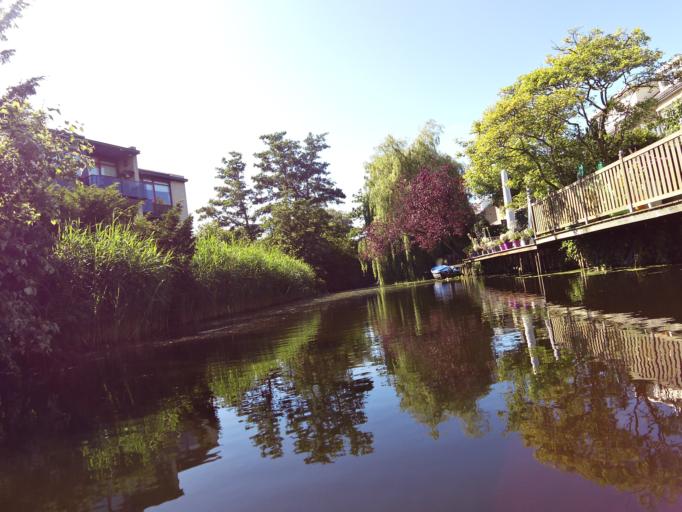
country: NL
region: South Holland
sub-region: Gemeente Wassenaar
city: Wassenaar
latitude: 52.1425
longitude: 4.4057
